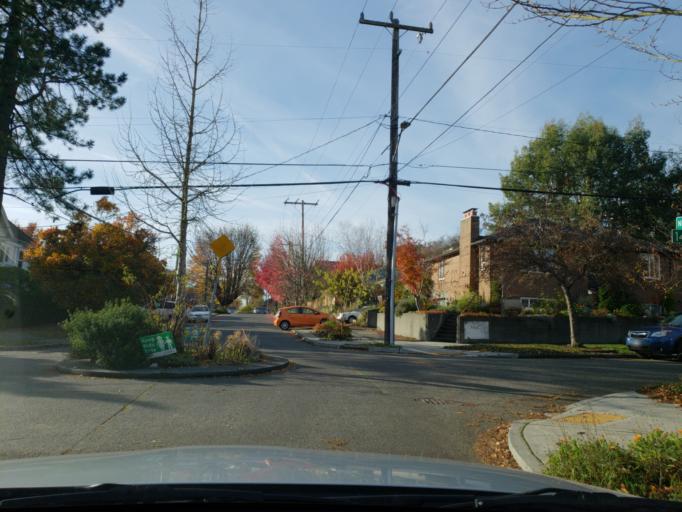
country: US
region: Washington
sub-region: King County
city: Shoreline
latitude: 47.6814
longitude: -122.3735
